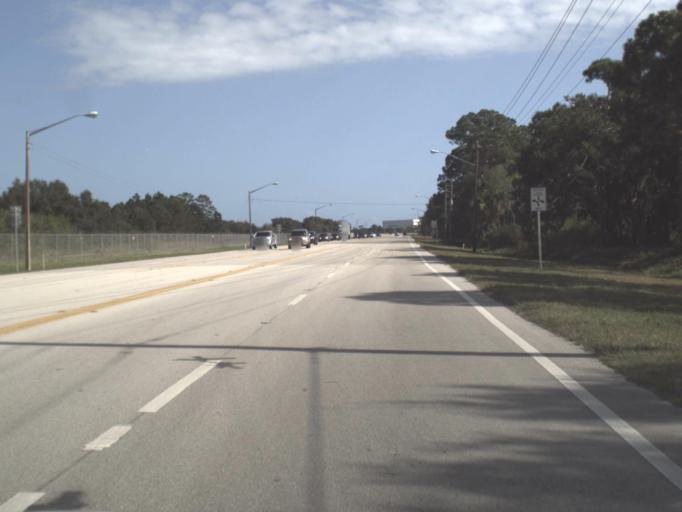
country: US
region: Florida
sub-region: Brevard County
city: West Melbourne
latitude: 28.0978
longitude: -80.6647
